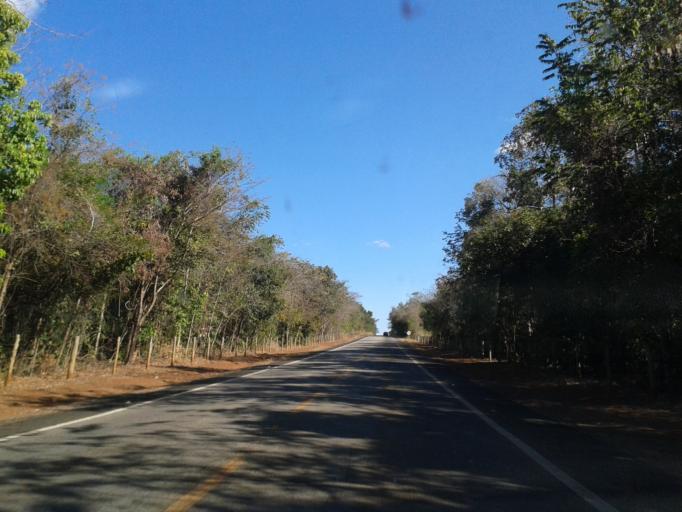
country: BR
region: Goias
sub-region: Mozarlandia
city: Mozarlandia
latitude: -14.6738
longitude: -50.5357
